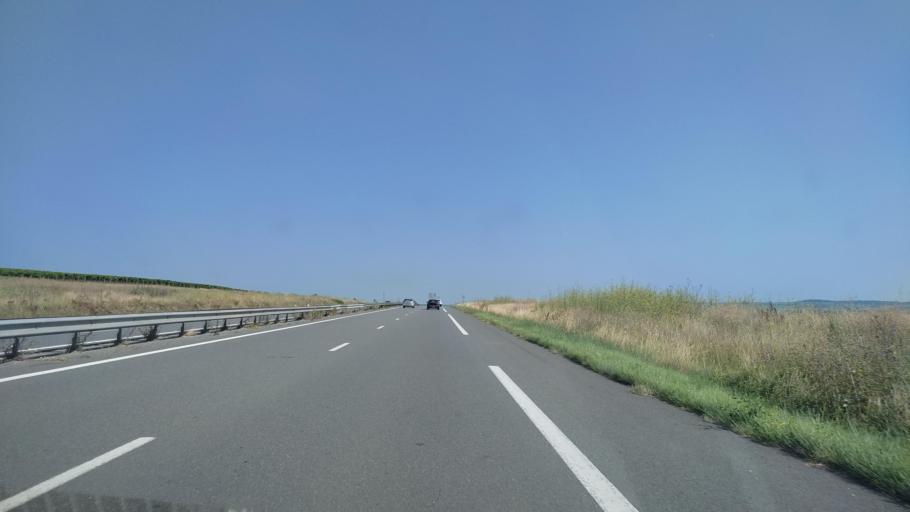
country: FR
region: Poitou-Charentes
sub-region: Departement de la Charente
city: Gensac-la-Pallue
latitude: 45.6665
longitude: -0.2446
